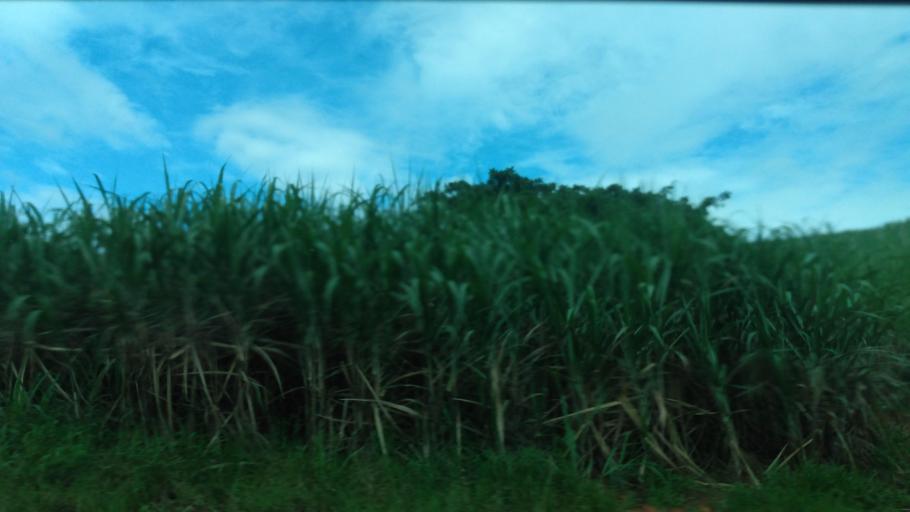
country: BR
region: Pernambuco
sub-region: Maraial
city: Maraial
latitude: -8.7157
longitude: -35.7767
